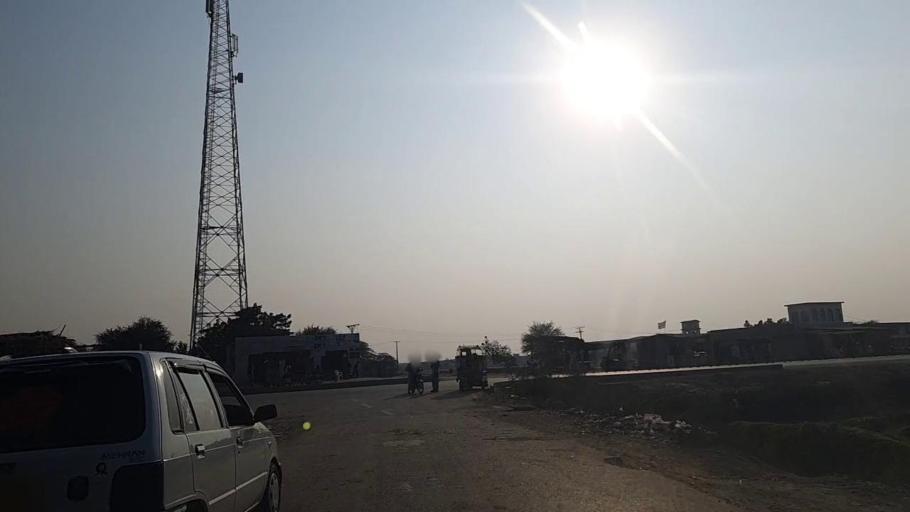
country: PK
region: Sindh
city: Shahpur Chakar
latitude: 26.1995
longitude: 68.5559
